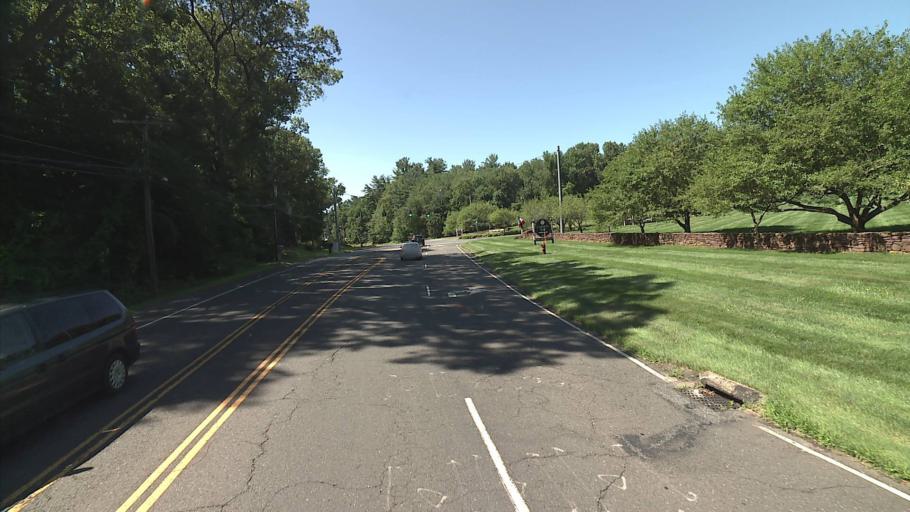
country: US
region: Connecticut
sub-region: Hartford County
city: Weatogue
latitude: 41.8552
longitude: -72.8121
